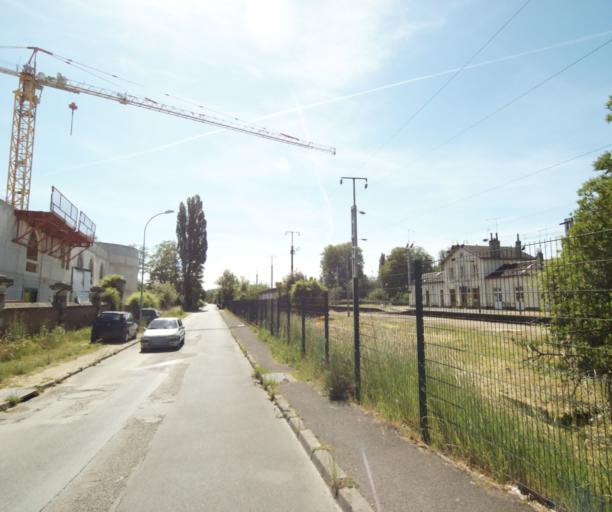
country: FR
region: Champagne-Ardenne
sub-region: Departement des Ardennes
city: Villers-Semeuse
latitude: 49.7531
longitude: 4.7330
